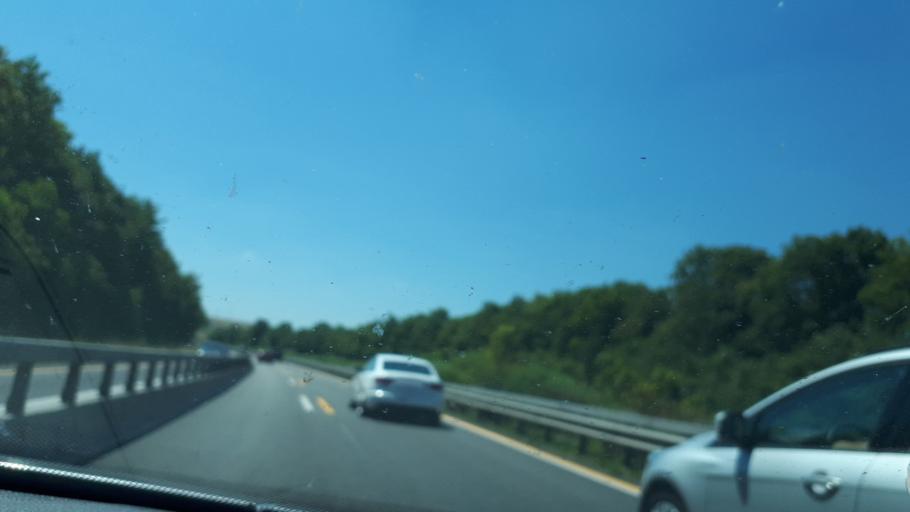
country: DE
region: Rheinland-Pfalz
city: Kehrig
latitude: 50.2657
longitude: 7.2255
